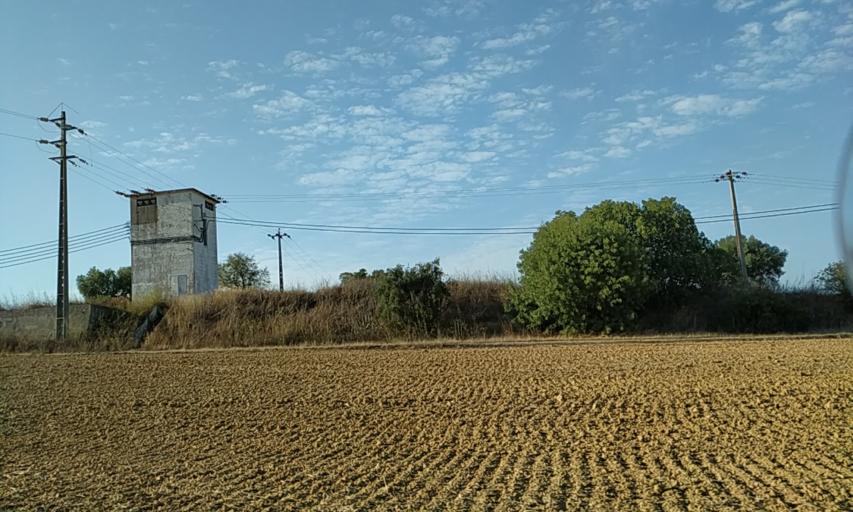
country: PT
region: Santarem
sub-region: Alcanena
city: Alcanena
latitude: 39.3471
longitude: -8.6628
